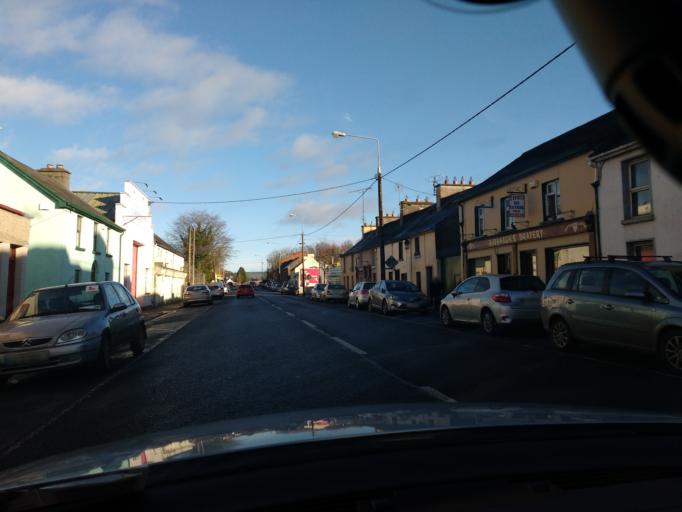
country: IE
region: Leinster
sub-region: Laois
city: Rathdowney
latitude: 52.7209
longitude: -7.5816
